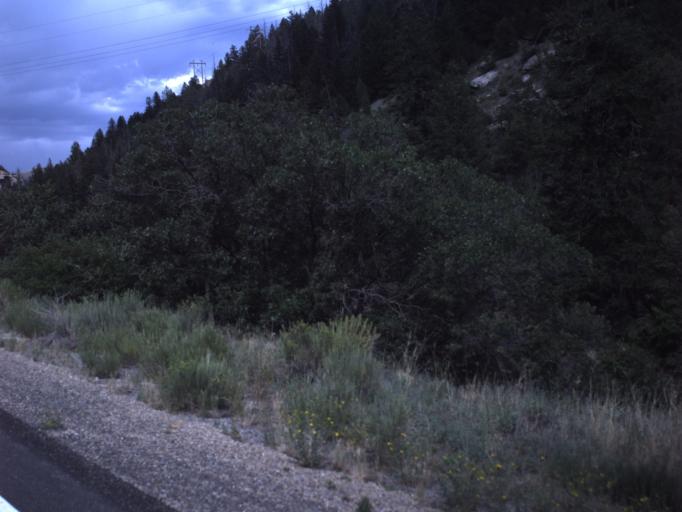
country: US
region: Utah
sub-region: Carbon County
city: Helper
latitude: 39.7542
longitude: -110.8254
